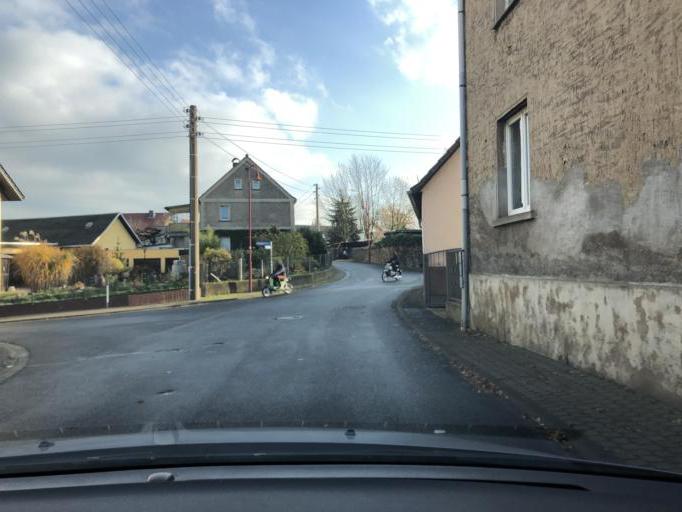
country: DE
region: Saxony
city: Grimma
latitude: 51.2532
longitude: 12.7314
